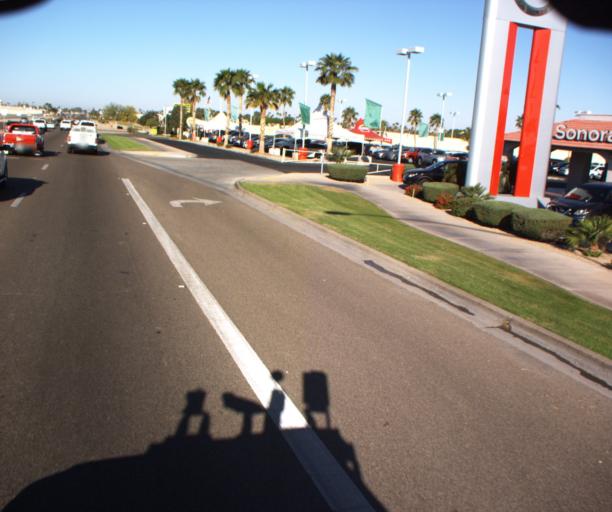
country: US
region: Arizona
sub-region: Yuma County
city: Yuma
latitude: 32.6695
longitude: -114.5996
